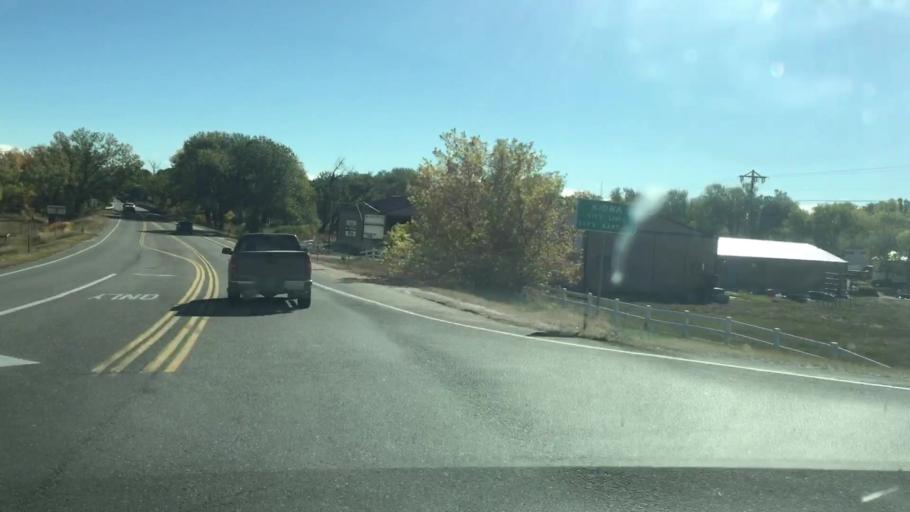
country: US
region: Colorado
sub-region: Elbert County
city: Kiowa
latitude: 39.3466
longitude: -104.4735
